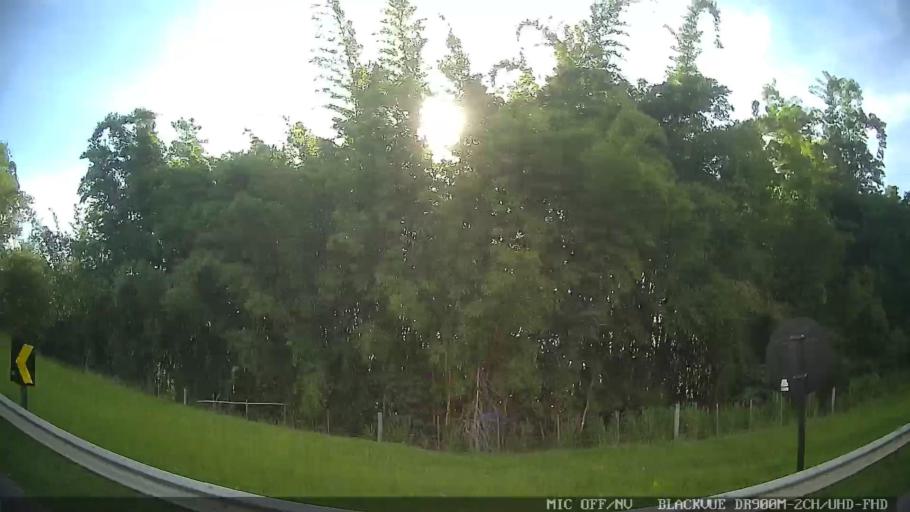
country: BR
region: Sao Paulo
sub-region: Tiete
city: Tiete
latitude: -23.1071
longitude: -47.7639
